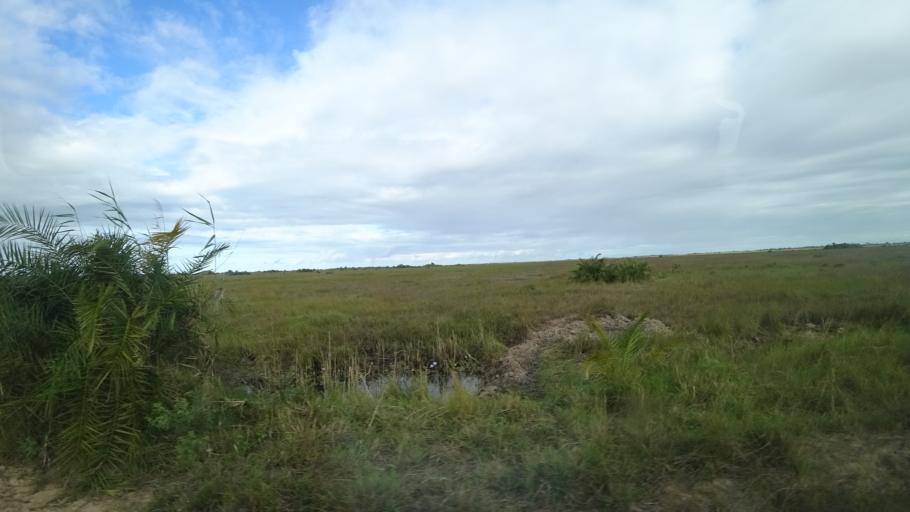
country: MZ
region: Sofala
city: Beira
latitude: -19.6838
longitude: 35.0524
